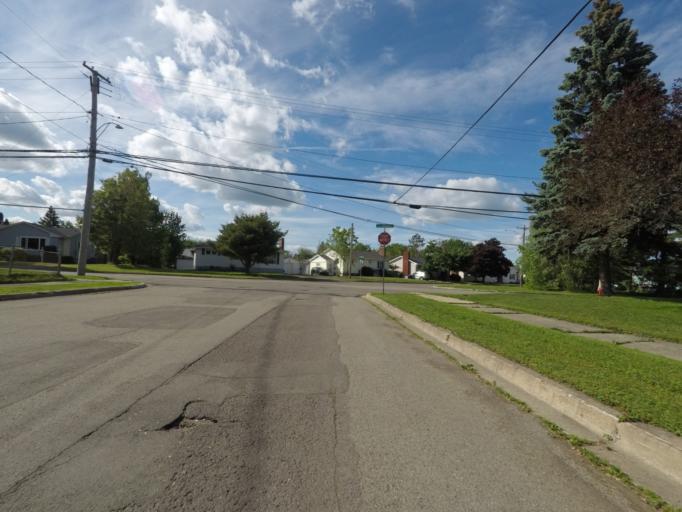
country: CA
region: New Brunswick
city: Moncton
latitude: 46.1033
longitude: -64.8266
